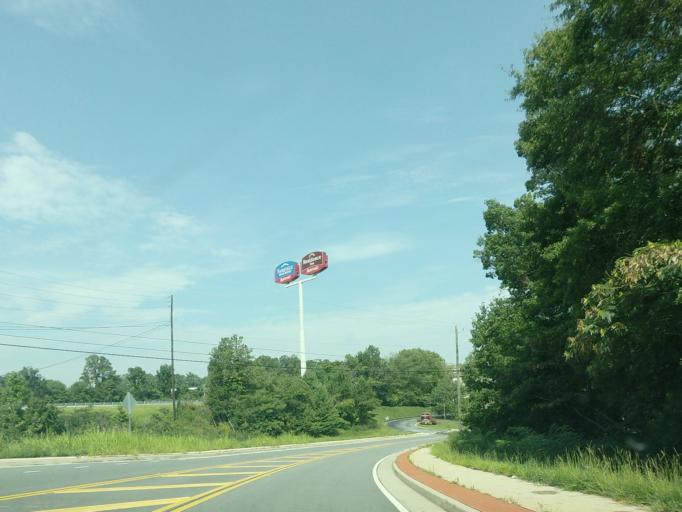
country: US
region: Georgia
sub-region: Bibb County
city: Macon
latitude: 32.9053
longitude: -83.6878
